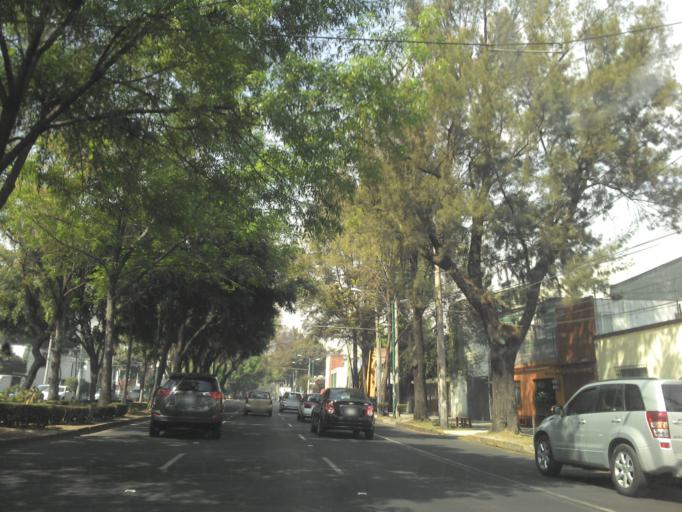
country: MX
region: Mexico City
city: Coyoacan
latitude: 19.3449
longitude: -99.1652
